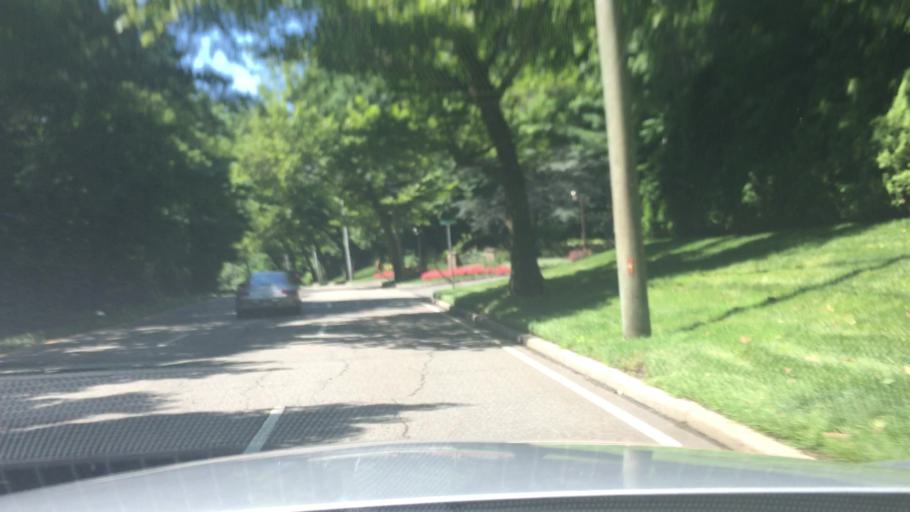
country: US
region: New York
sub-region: Nassau County
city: Searingtown
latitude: 40.7788
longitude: -73.6656
